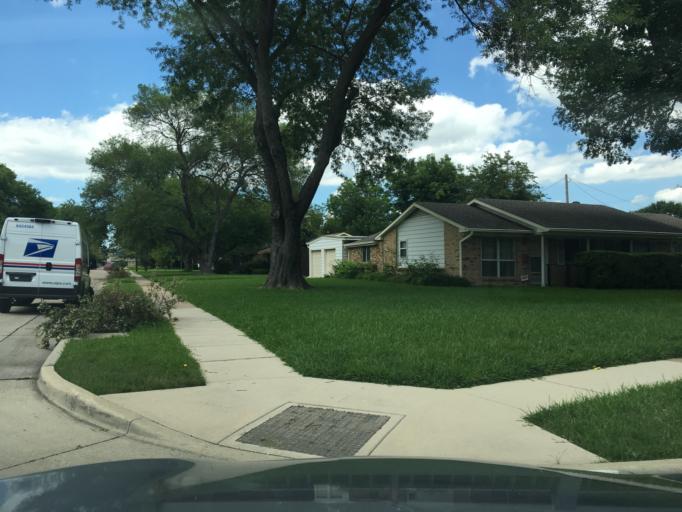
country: US
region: Texas
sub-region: Dallas County
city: Richardson
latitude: 32.9476
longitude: -96.7092
